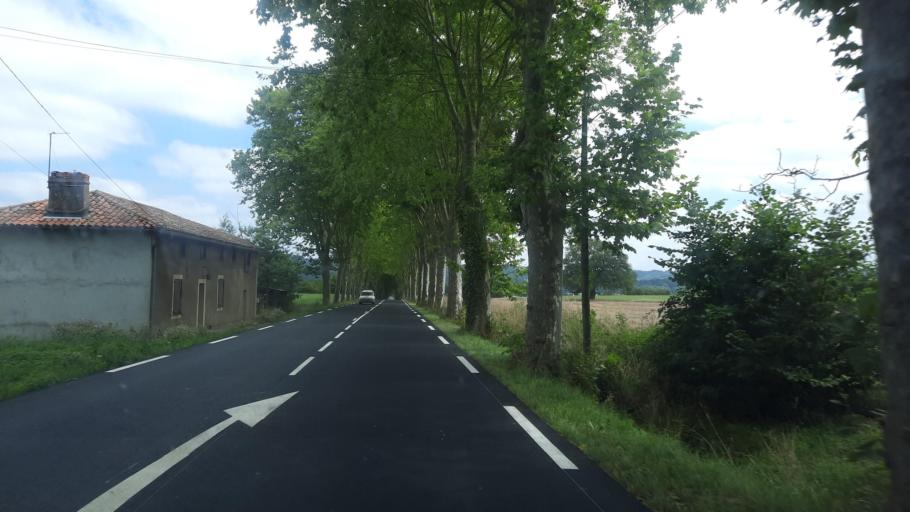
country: FR
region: Midi-Pyrenees
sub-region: Departement de la Haute-Garonne
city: Boulogne-sur-Gesse
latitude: 43.2928
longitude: 0.5200
